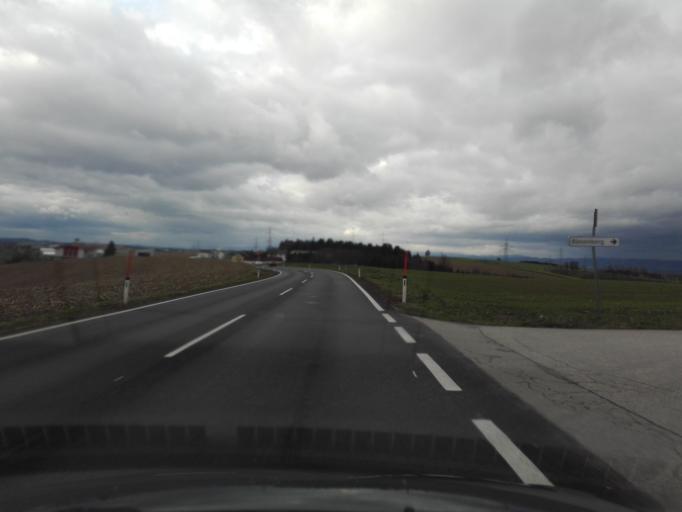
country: AT
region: Lower Austria
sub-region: Politischer Bezirk Amstetten
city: Wolfsbach
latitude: 48.1238
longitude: 14.7165
